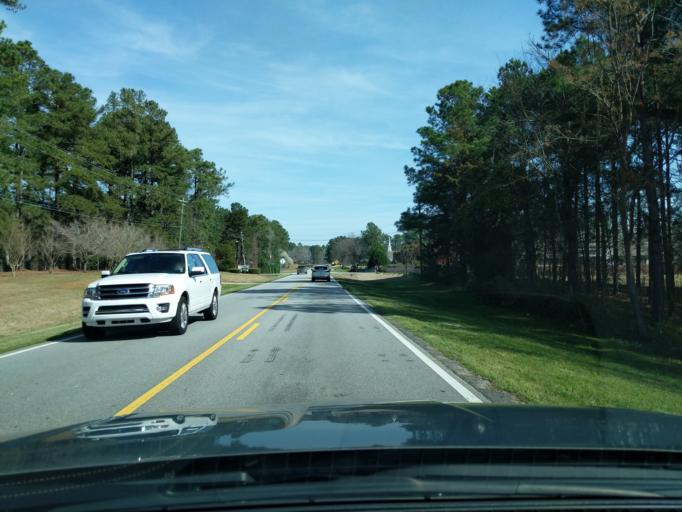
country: US
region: Georgia
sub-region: Columbia County
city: Evans
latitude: 33.5560
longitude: -82.1280
